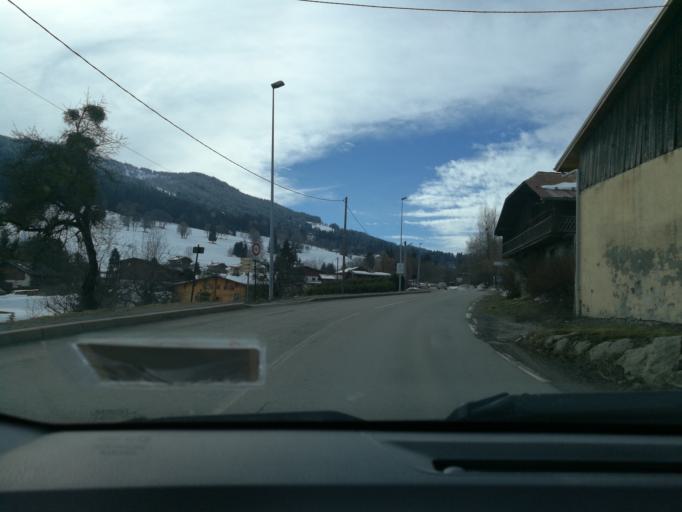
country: FR
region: Rhone-Alpes
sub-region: Departement de la Haute-Savoie
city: Combloux
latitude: 45.8874
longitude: 6.6448
